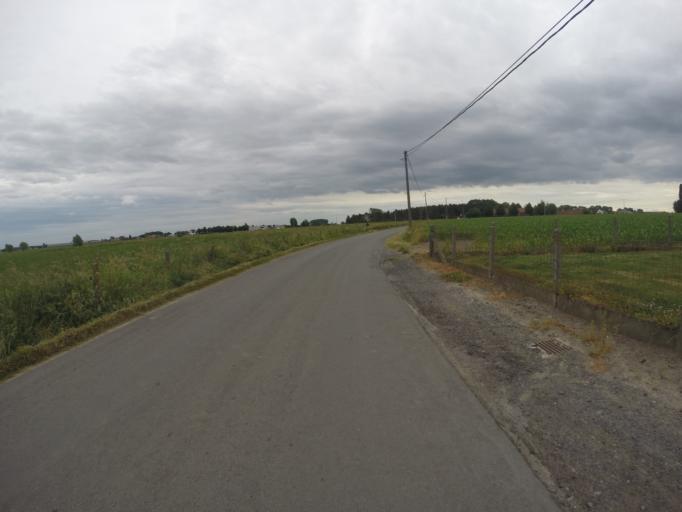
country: BE
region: Flanders
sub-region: Provincie West-Vlaanderen
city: Ruiselede
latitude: 51.0606
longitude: 3.3599
